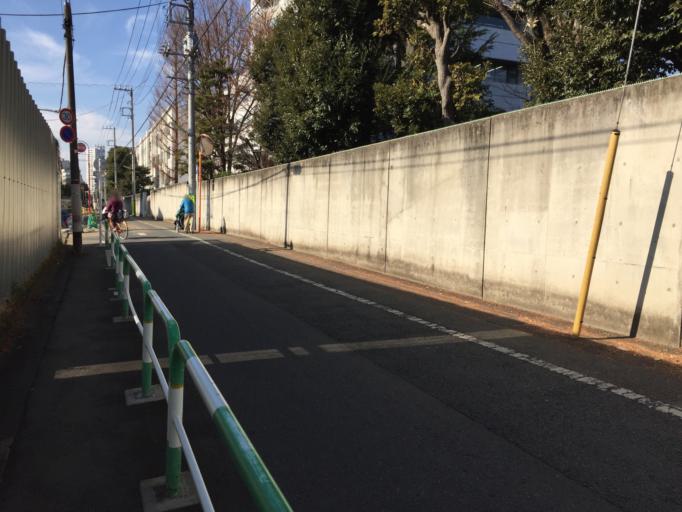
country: JP
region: Tokyo
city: Tokyo
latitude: 35.6436
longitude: 139.6776
